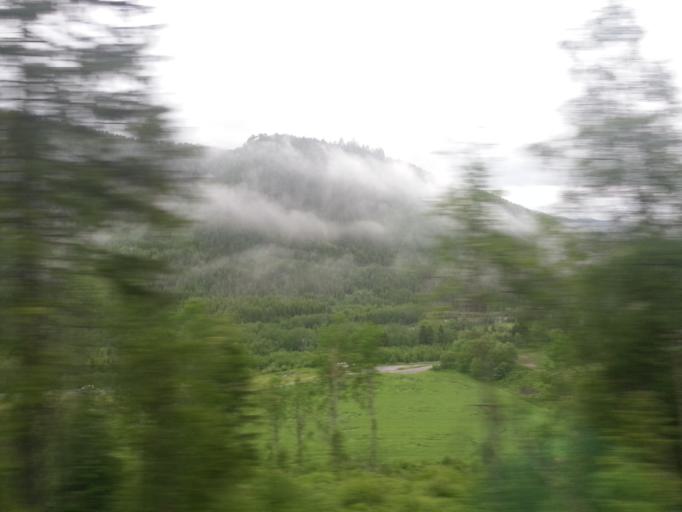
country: NO
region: Sor-Trondelag
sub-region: Midtre Gauldal
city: Storen
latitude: 63.0038
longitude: 10.2331
